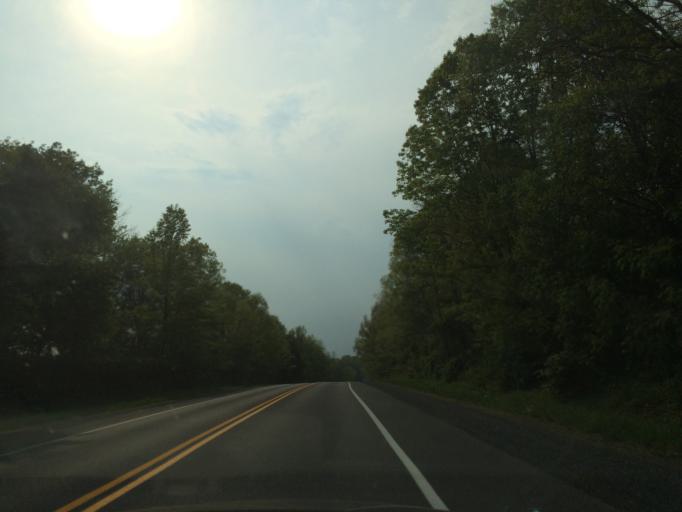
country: US
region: Maryland
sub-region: Carroll County
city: Mount Airy
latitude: 39.3494
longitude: -77.1030
